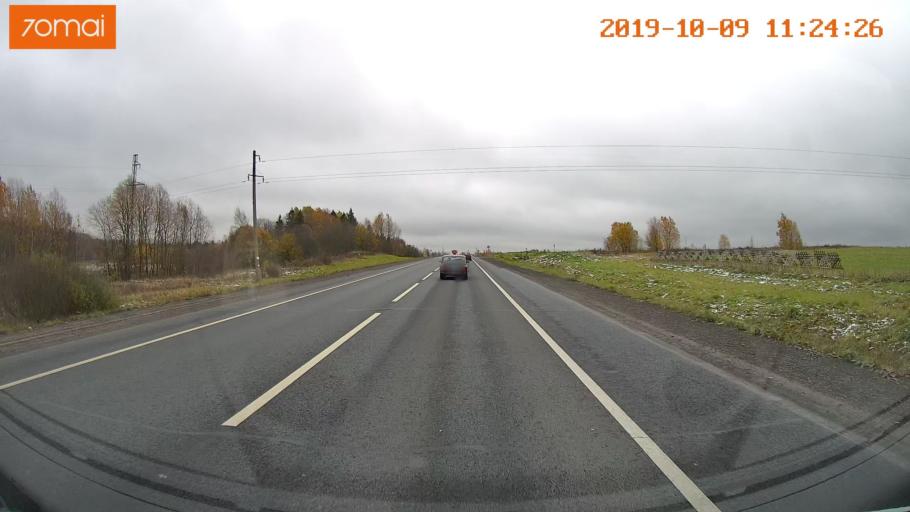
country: RU
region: Vologda
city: Vologda
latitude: 59.1115
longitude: 39.9799
